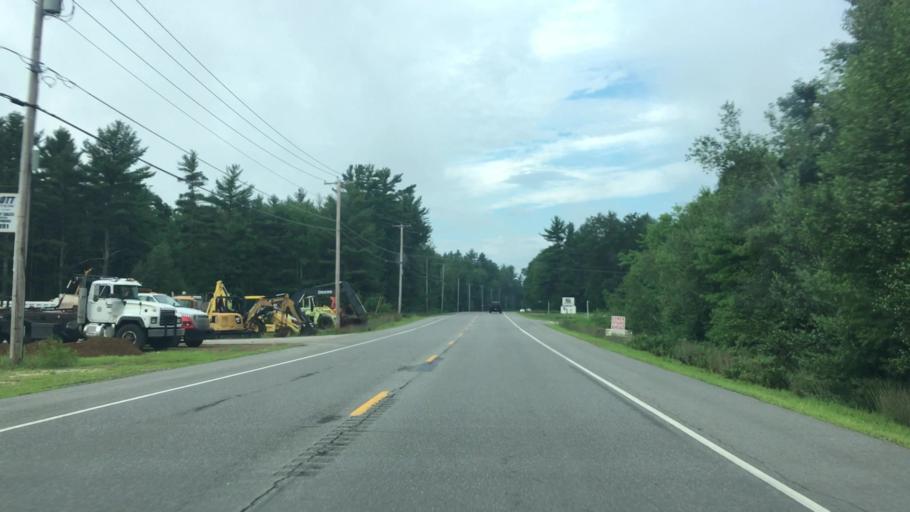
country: US
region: Maine
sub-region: York County
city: Lebanon
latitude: 43.3714
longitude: -70.8918
